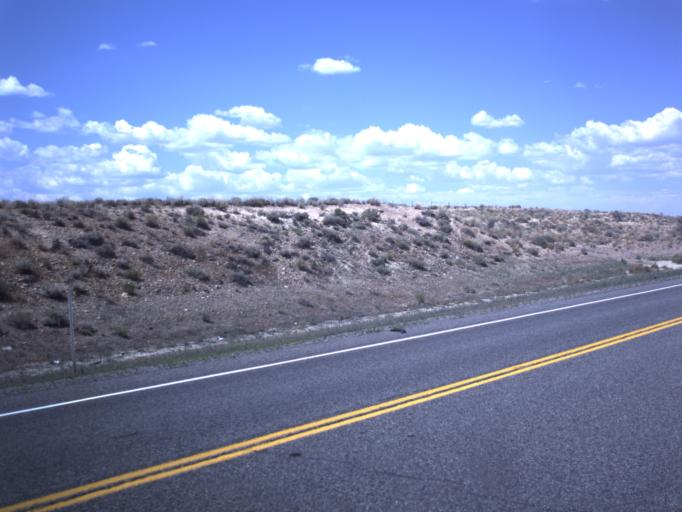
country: US
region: Utah
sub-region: Emery County
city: Huntington
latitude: 39.3879
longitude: -110.9021
